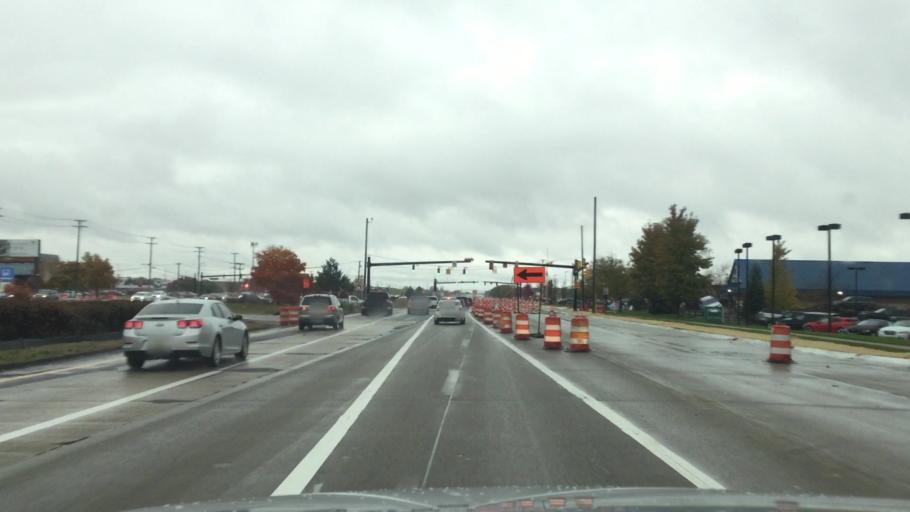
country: US
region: Michigan
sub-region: Macomb County
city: Clinton
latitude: 42.6287
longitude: -82.9322
